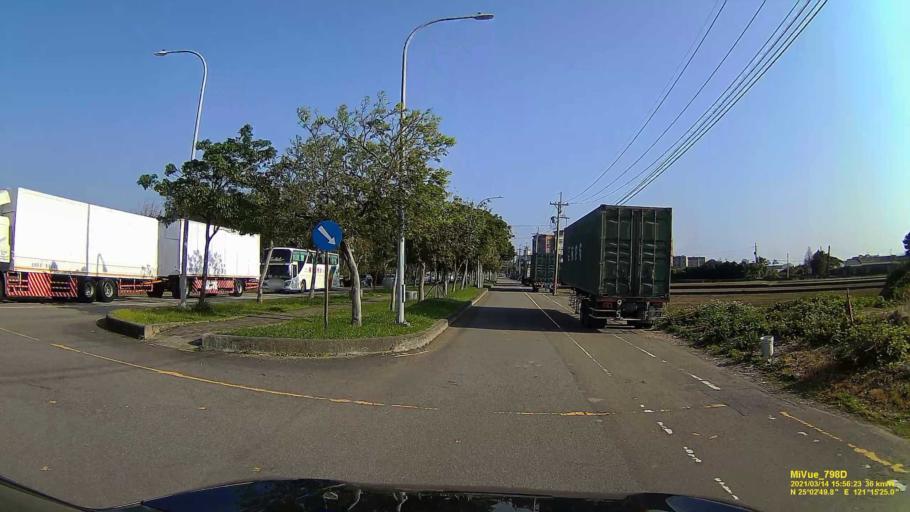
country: TW
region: Taiwan
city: Taoyuan City
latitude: 25.0470
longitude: 121.2570
